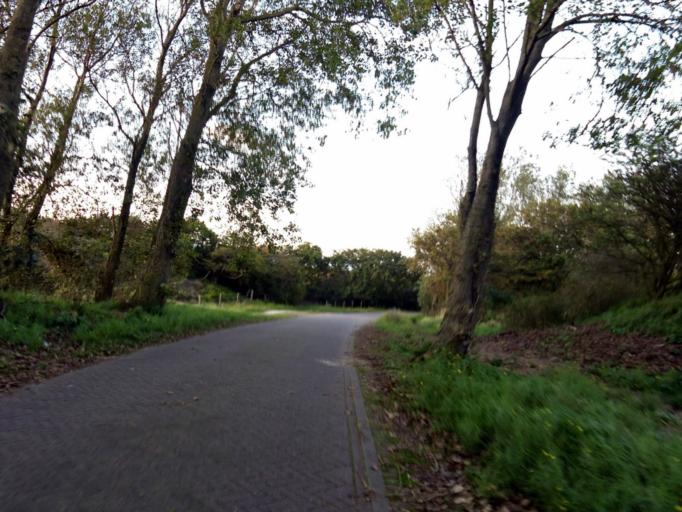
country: NL
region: South Holland
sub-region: Gemeente Den Haag
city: Scheveningen
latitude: 52.1379
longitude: 4.3334
